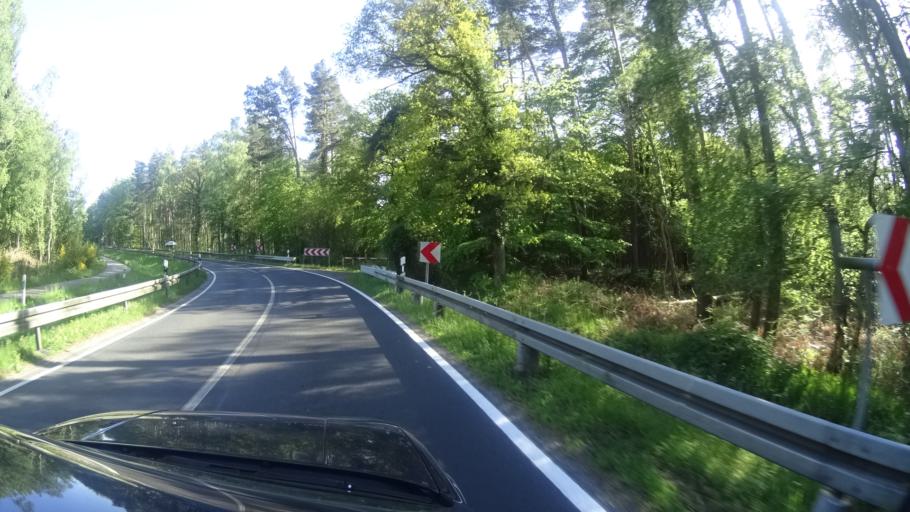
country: DE
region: Mecklenburg-Vorpommern
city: Ostseebad Prerow
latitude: 54.4240
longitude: 12.5718
